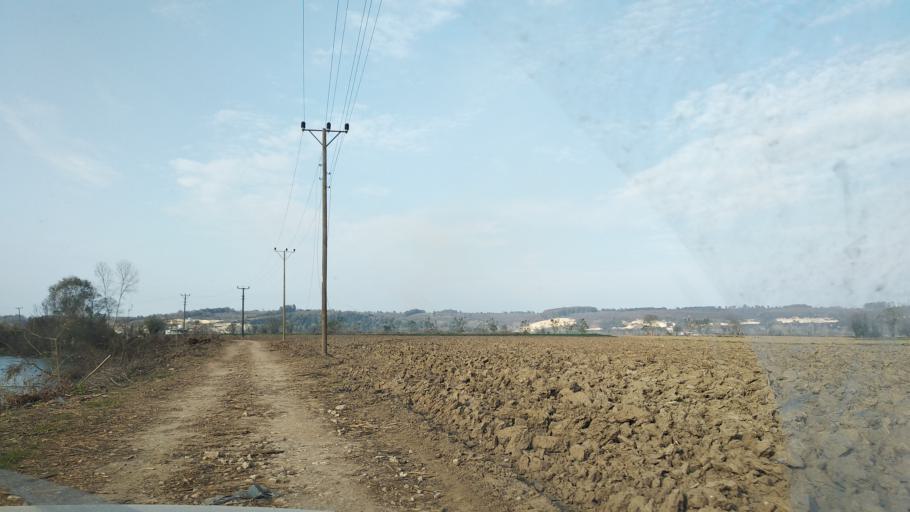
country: TR
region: Sakarya
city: Karasu
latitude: 41.0853
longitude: 30.6021
